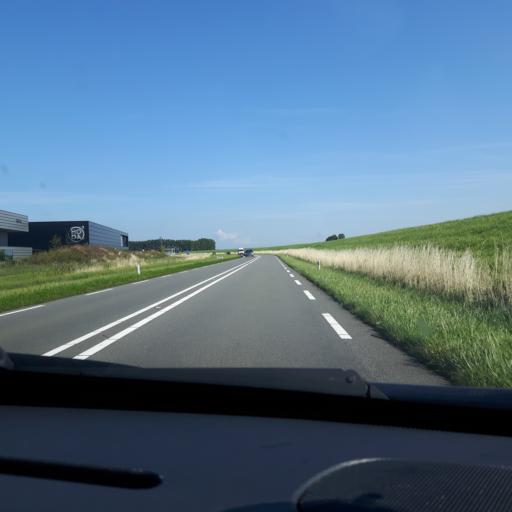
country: NL
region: Zeeland
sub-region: Schouwen-Duiveland
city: Scharendijke
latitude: 51.6397
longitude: 3.9374
